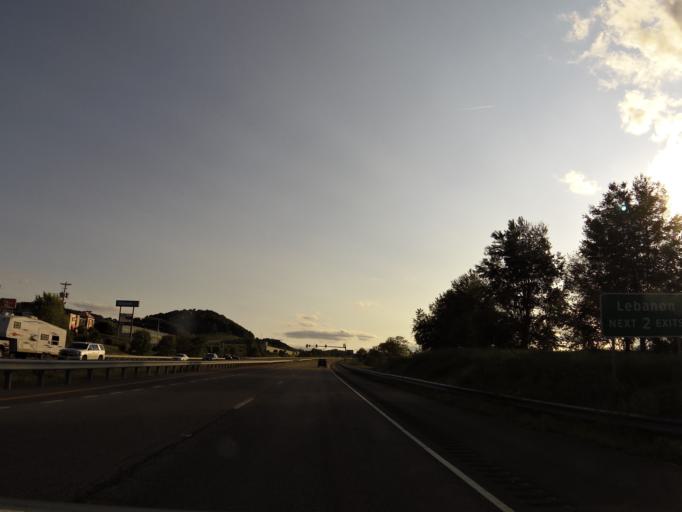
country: US
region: Virginia
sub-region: Russell County
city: Lebanon
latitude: 36.9037
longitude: -82.0452
